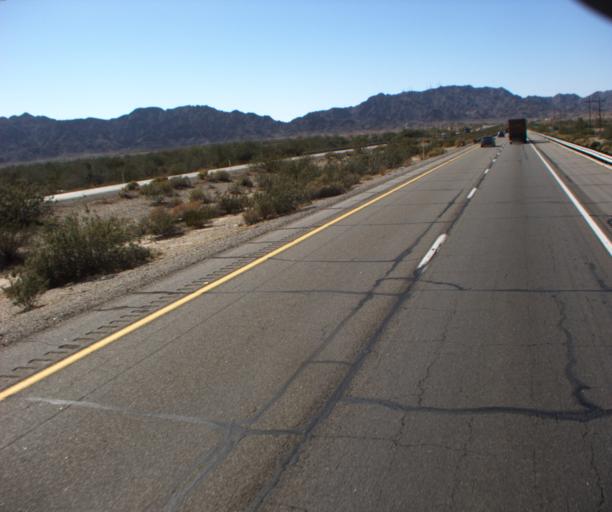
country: US
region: Arizona
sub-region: Yuma County
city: Wellton
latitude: 32.6639
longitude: -114.2703
